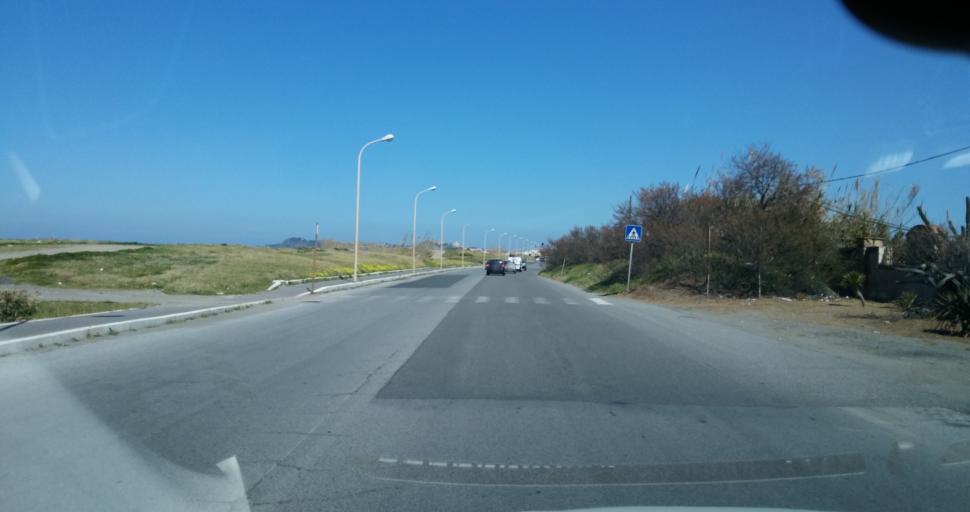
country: IT
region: Sicily
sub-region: Messina
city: Milazzo
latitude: 38.1914
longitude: 15.2174
